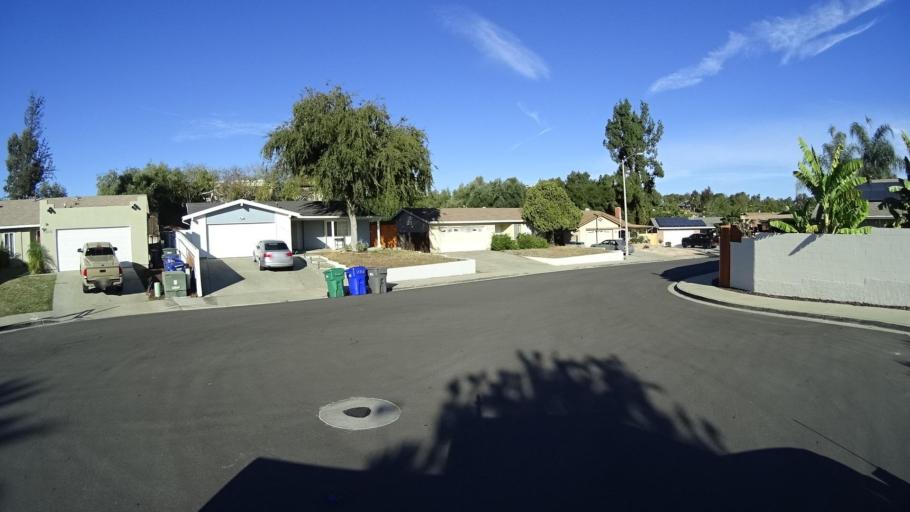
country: US
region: California
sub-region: San Diego County
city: Lakeside
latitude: 32.8425
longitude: -116.9052
